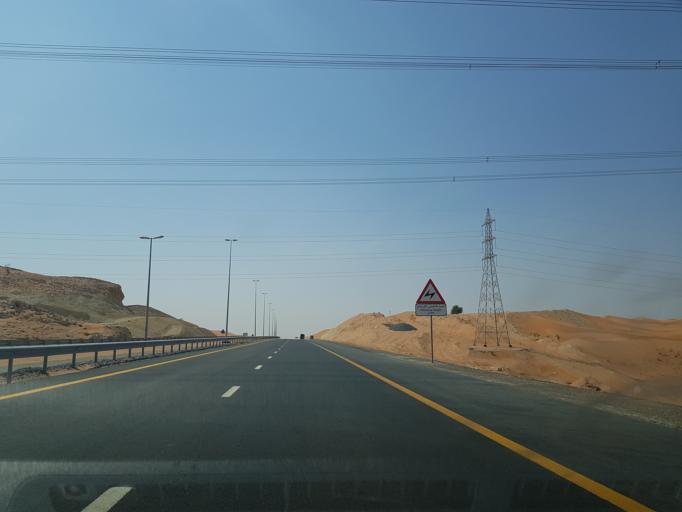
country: AE
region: Ash Shariqah
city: Adh Dhayd
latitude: 25.2468
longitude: 55.8450
